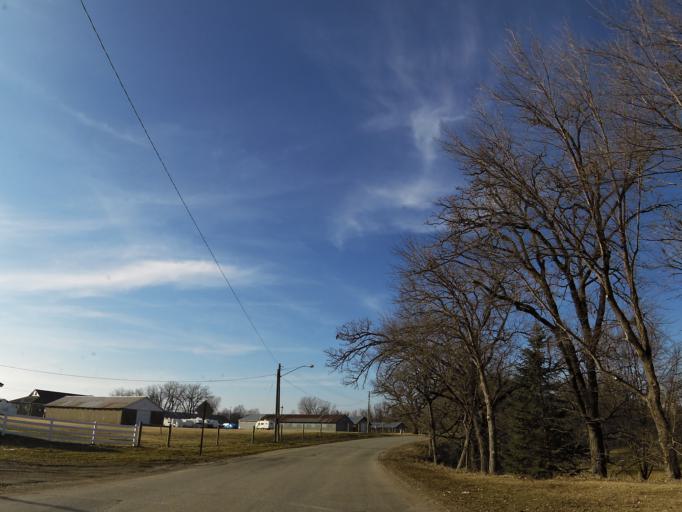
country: US
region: Minnesota
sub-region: Goodhue County
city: Cannon Falls
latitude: 44.5134
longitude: -92.9122
